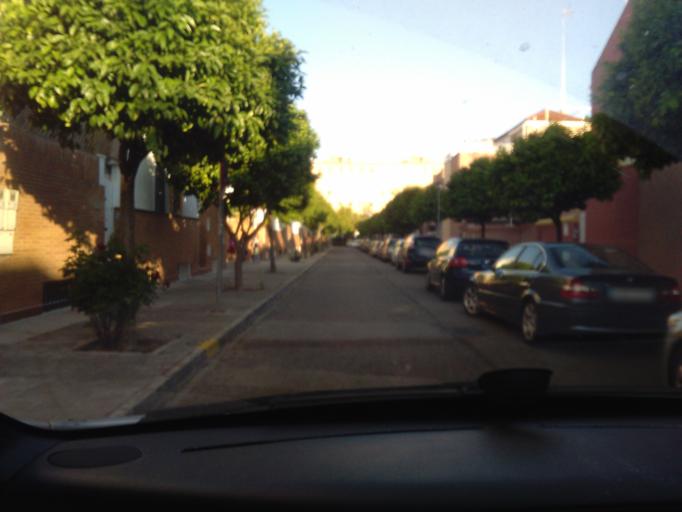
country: ES
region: Andalusia
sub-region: Provincia de Sevilla
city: Sevilla
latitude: 37.4041
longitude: -5.9437
